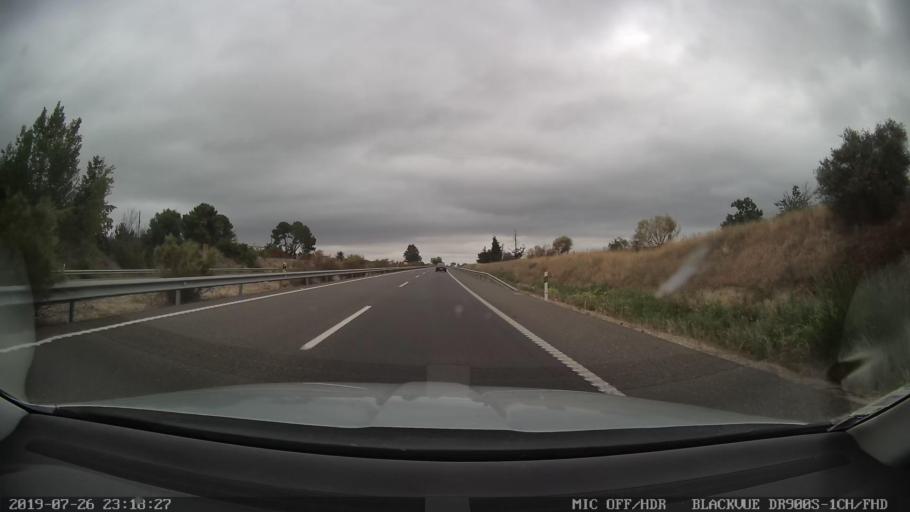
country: ES
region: Extremadura
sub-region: Provincia de Badajoz
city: Santa Amalia
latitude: 39.0956
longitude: -6.0121
